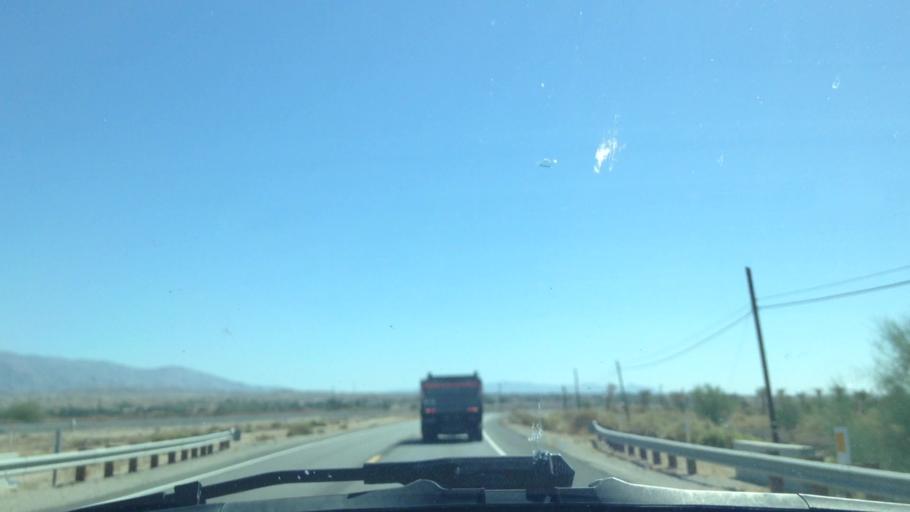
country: US
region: California
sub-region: Riverside County
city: Mecca
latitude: 33.5323
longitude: -115.9523
